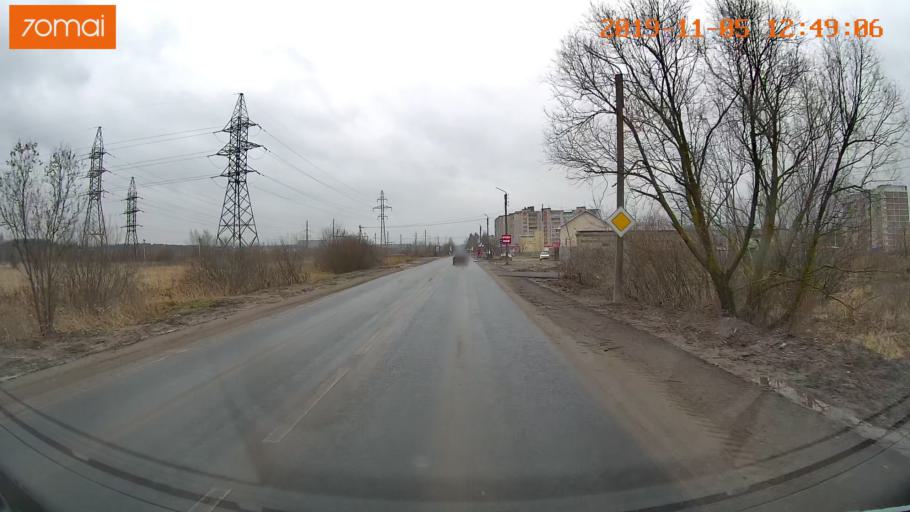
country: RU
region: Ivanovo
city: Kokhma
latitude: 56.9568
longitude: 41.1023
